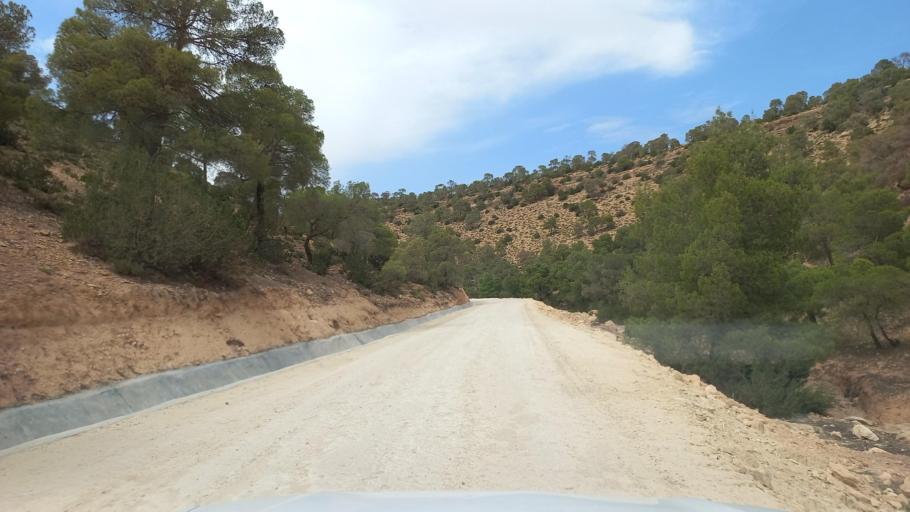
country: TN
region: Al Qasrayn
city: Kasserine
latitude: 35.3756
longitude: 8.8872
